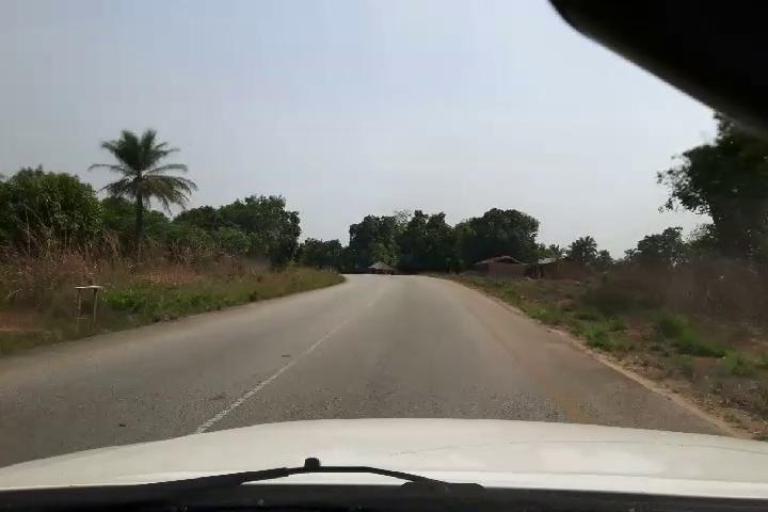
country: SL
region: Southern Province
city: Largo
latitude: 8.3114
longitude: -12.2159
